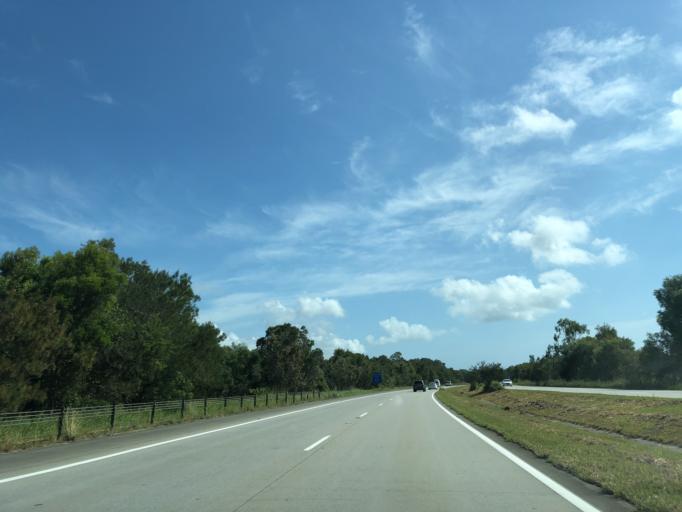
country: AU
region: New South Wales
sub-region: Byron Shire
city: Brunswick Heads
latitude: -28.5689
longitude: 153.5406
